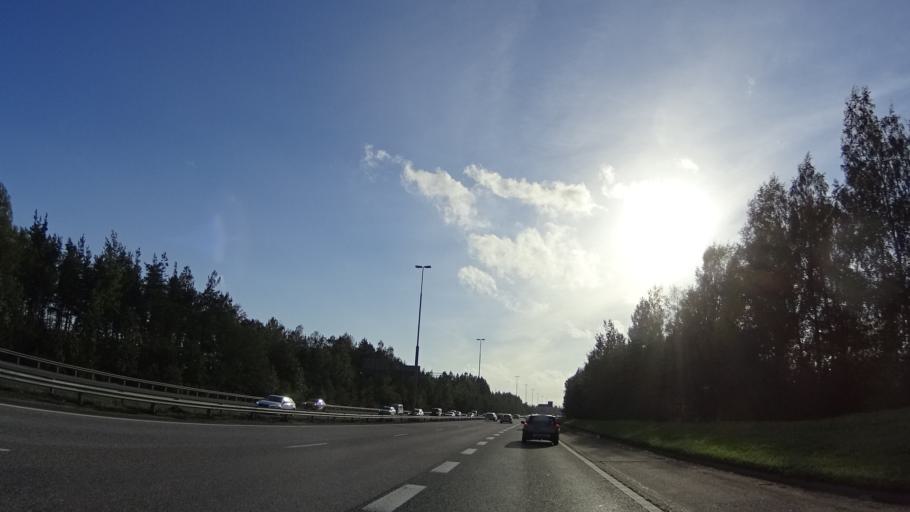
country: FI
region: Uusimaa
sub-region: Helsinki
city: Vantaa
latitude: 60.2460
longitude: 25.0581
